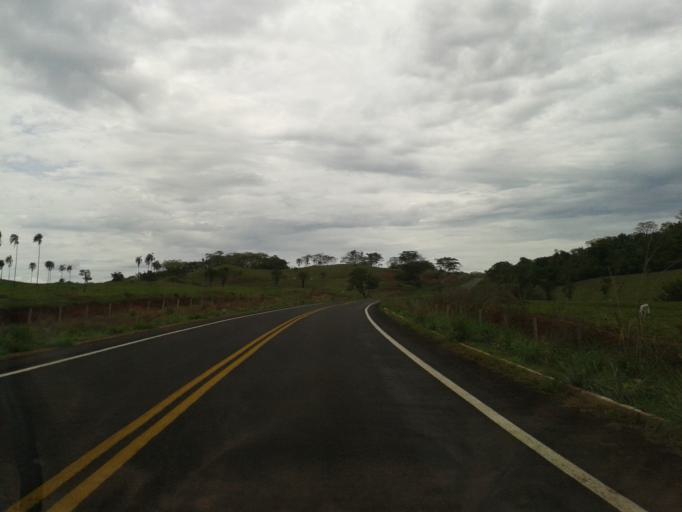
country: BR
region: Goias
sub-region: Buriti Alegre
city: Buriti Alegre
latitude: -18.1393
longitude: -48.8912
